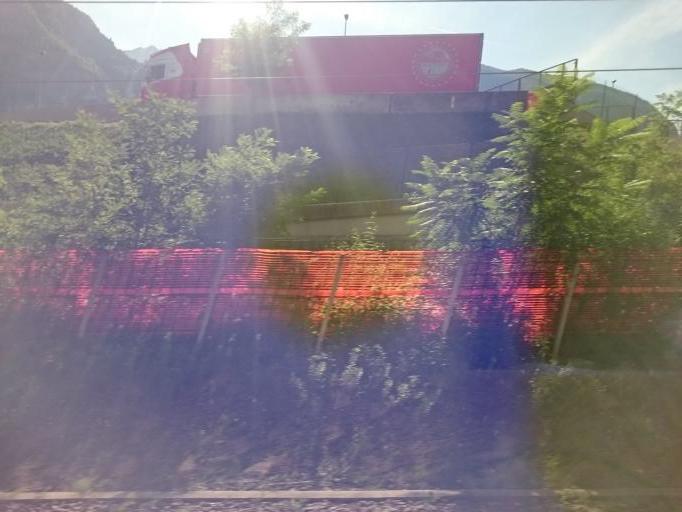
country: IT
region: Trentino-Alto Adige
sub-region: Provincia di Trento
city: Besenello
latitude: 45.9494
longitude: 11.1054
